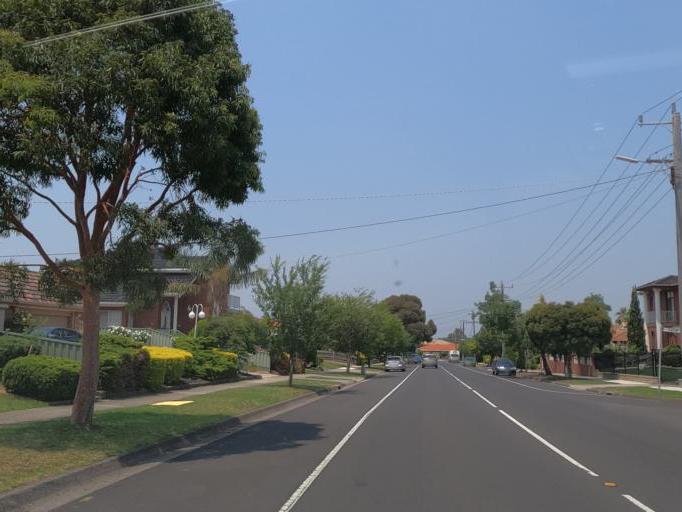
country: AU
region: Victoria
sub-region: Hume
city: Greenvale
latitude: -37.6402
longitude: 144.8920
